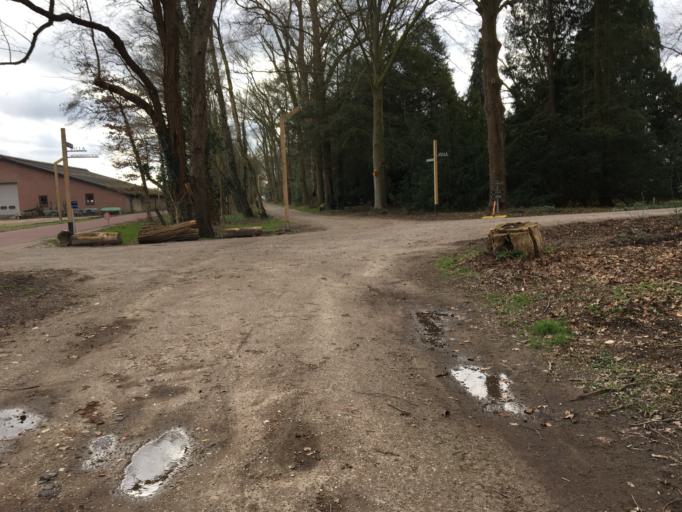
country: NL
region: Utrecht
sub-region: Gemeente Utrechtse Heuvelrug
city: Driebergen-Rijsenburg
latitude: 52.0618
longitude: 5.2620
